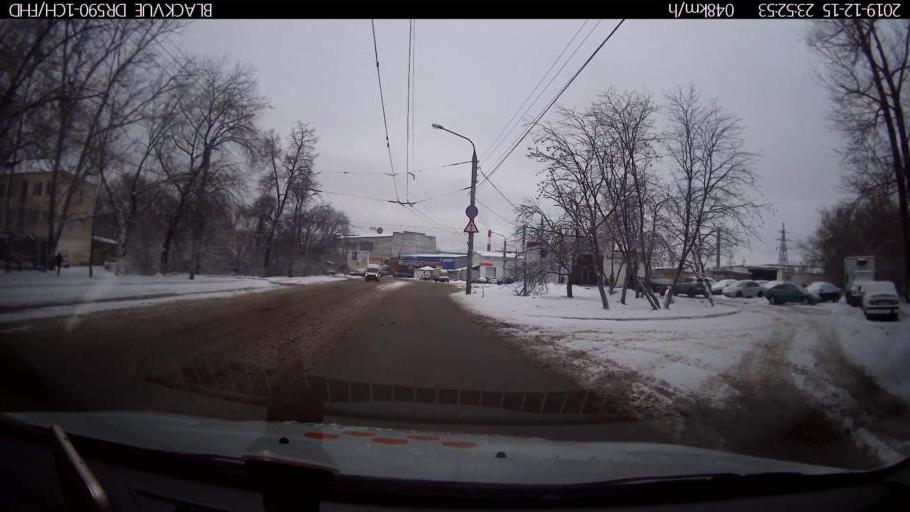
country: RU
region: Nizjnij Novgorod
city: Nizhniy Novgorod
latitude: 56.2730
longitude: 43.9377
